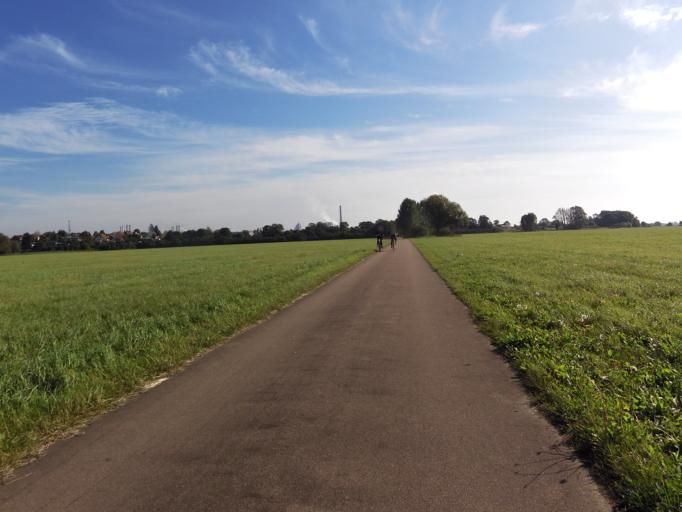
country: DE
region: Saxony-Anhalt
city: Nudersdorf
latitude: 51.8707
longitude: 12.5532
